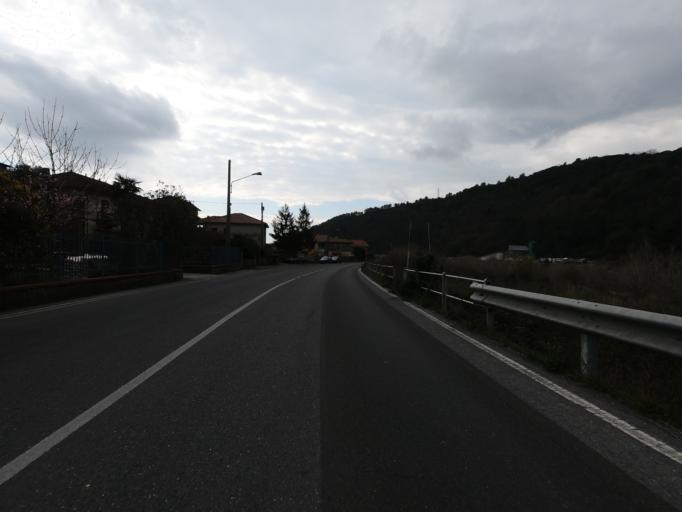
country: IT
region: Liguria
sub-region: Provincia di Savona
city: Laigueglia
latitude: 43.9897
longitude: 8.1226
